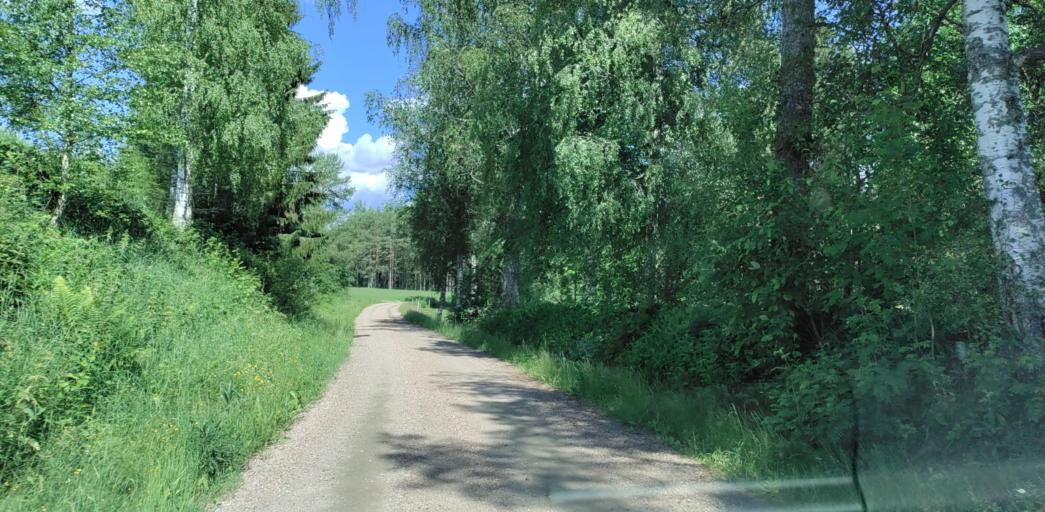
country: SE
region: Vaermland
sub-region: Munkfors Kommun
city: Munkfors
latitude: 59.9504
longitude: 13.4995
